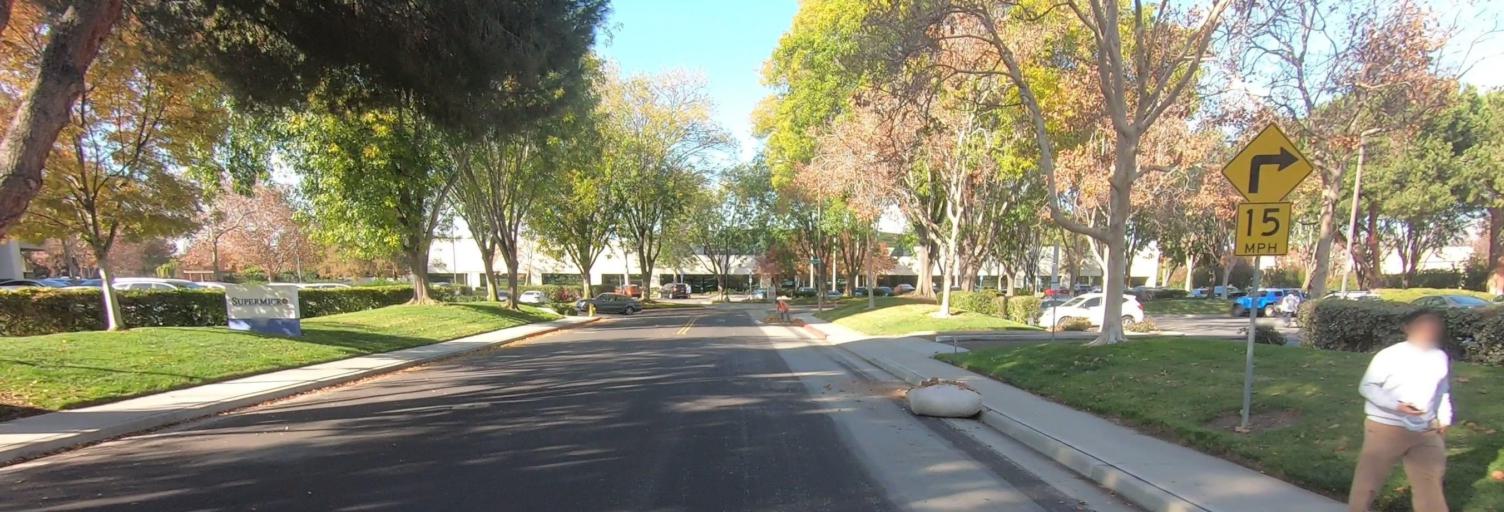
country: US
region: California
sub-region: Santa Clara County
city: Milpitas
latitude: 37.3861
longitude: -121.9037
